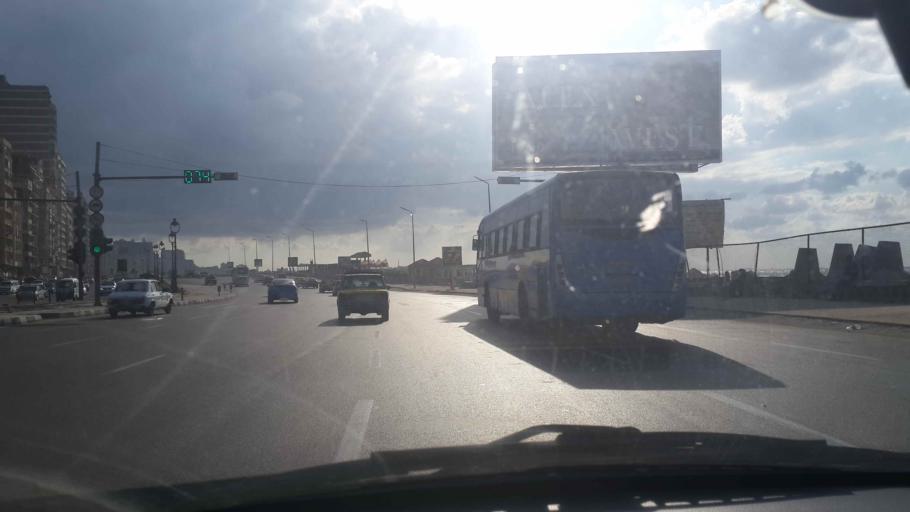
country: EG
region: Alexandria
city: Alexandria
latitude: 31.2275
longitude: 29.9388
